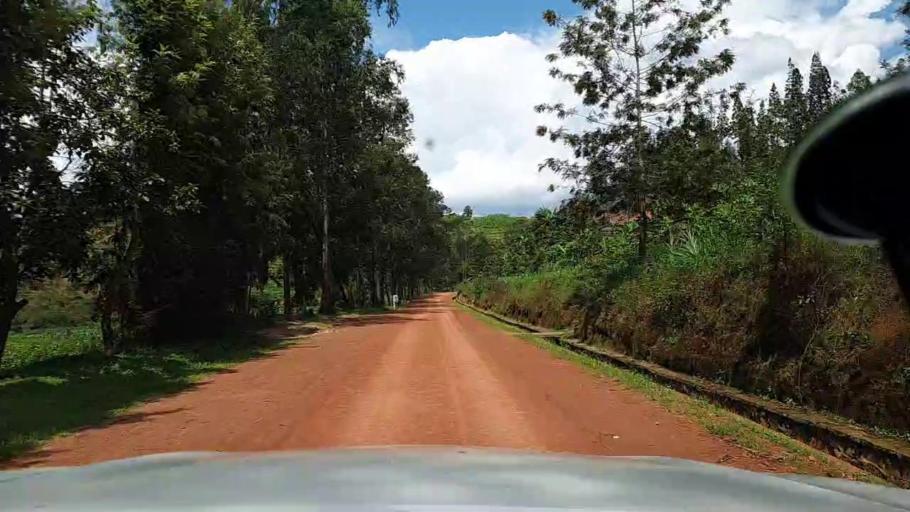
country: RW
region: Northern Province
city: Byumba
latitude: -1.6949
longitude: 29.8276
